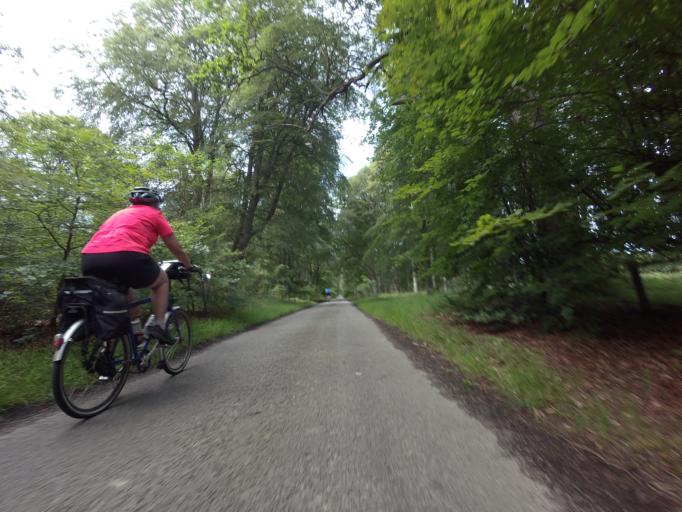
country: GB
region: Scotland
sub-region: Moray
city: Hopeman
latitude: 57.6713
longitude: -3.4129
